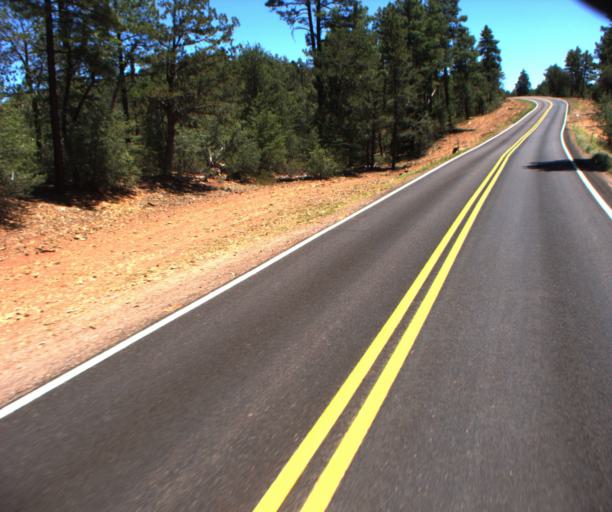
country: US
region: Arizona
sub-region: Gila County
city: Pine
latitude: 34.3661
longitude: -111.4335
